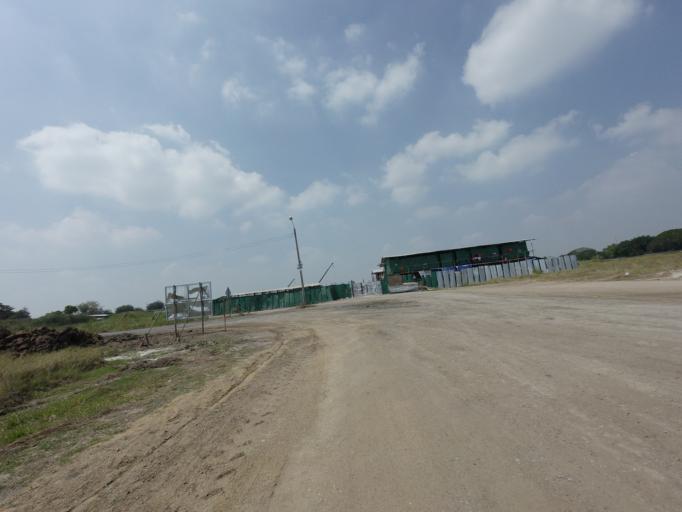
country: TH
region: Bangkok
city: Saphan Sung
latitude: 13.7521
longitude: 100.6747
